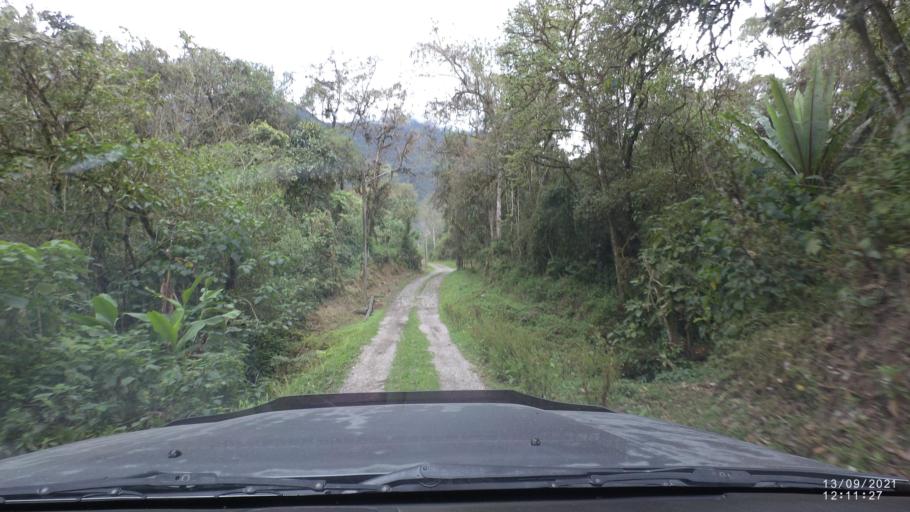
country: BO
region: Cochabamba
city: Colomi
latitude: -17.2144
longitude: -65.8257
